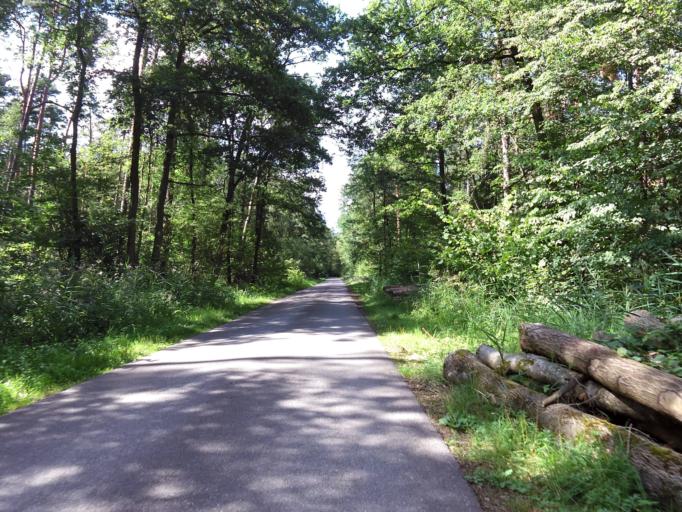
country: DE
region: Rheinland-Pfalz
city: Hanhofen
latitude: 49.3416
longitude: 8.3298
